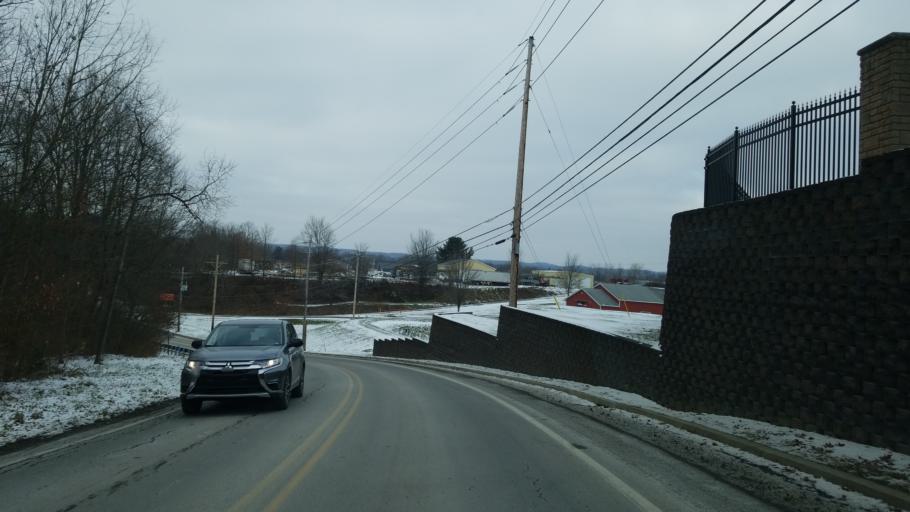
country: US
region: Pennsylvania
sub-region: Clearfield County
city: DuBois
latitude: 41.1062
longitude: -78.7324
